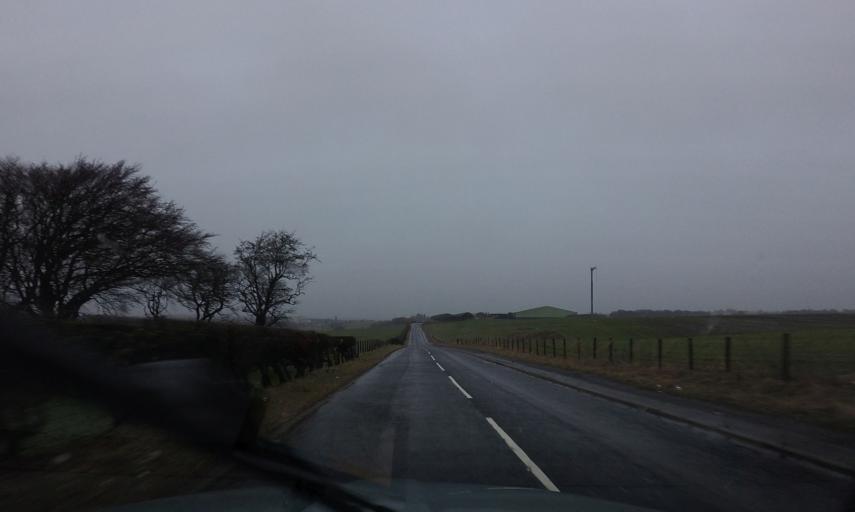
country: GB
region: Scotland
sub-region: North Lanarkshire
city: Shotts
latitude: 55.8099
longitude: -3.8055
